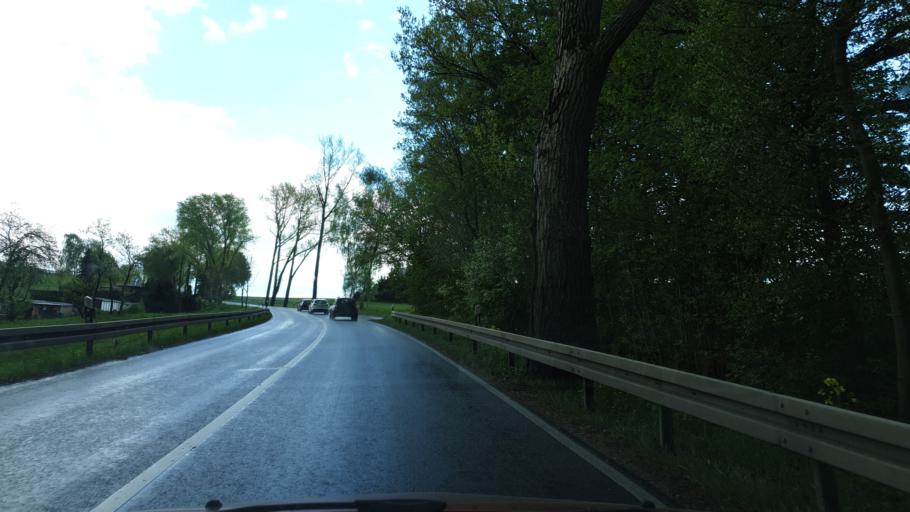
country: DE
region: Saxony
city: Neukirchen
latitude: 50.8071
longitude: 12.8240
